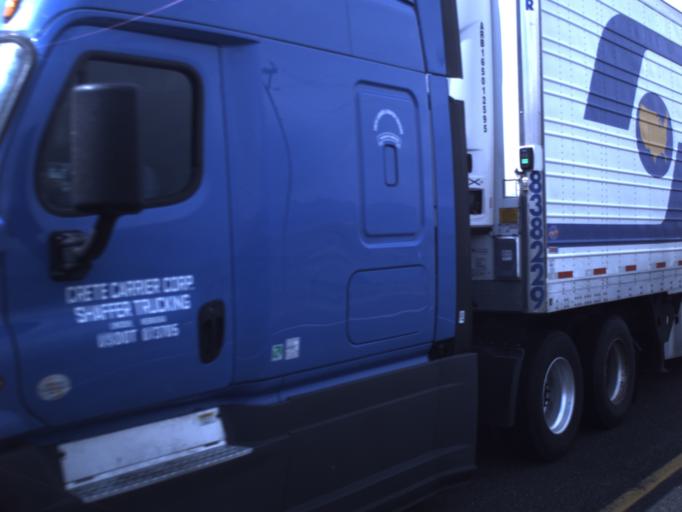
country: US
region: Utah
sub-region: Garfield County
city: Panguitch
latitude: 37.8553
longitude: -112.4387
